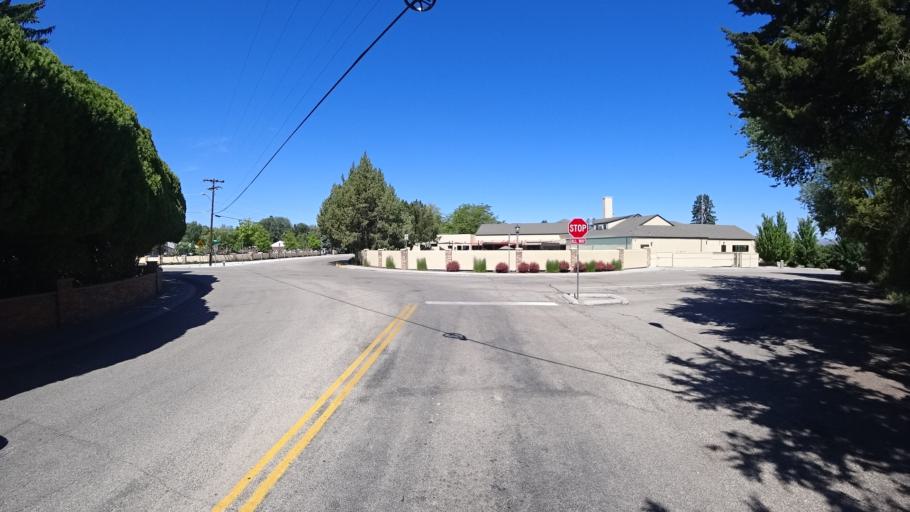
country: US
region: Idaho
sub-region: Ada County
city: Garden City
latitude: 43.5851
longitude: -116.2386
